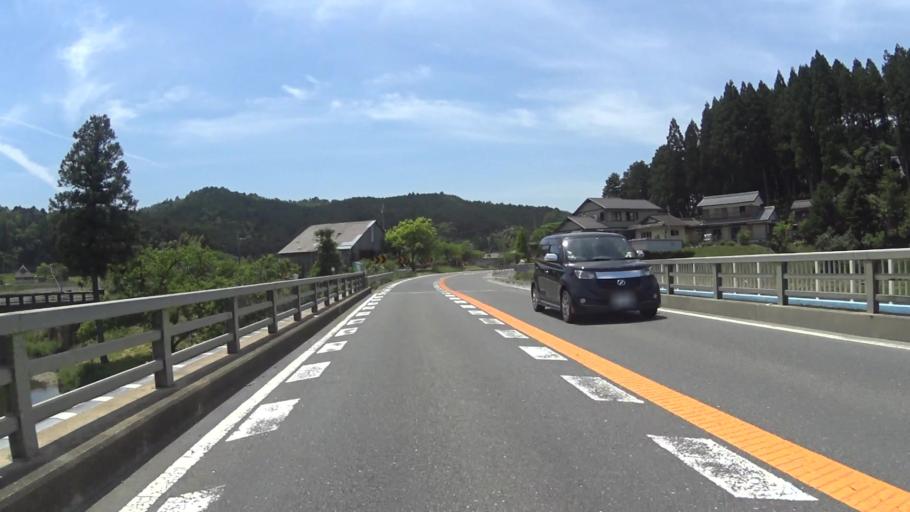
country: JP
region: Kyoto
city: Ayabe
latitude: 35.1880
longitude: 135.3151
